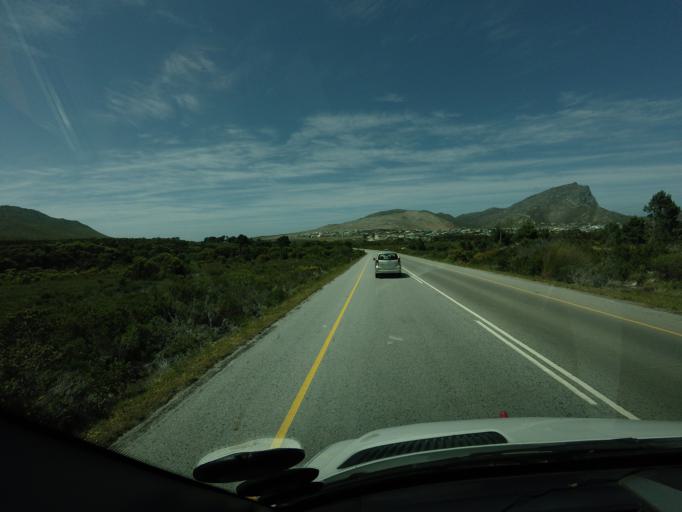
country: ZA
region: Western Cape
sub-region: Overberg District Municipality
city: Grabouw
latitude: -34.3316
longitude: 18.8393
